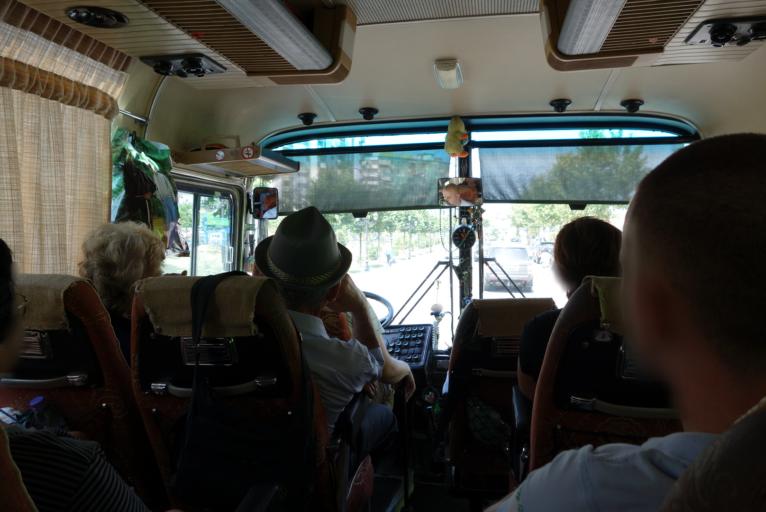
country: AL
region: Tirane
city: Tirana
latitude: 41.3211
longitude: 19.7946
